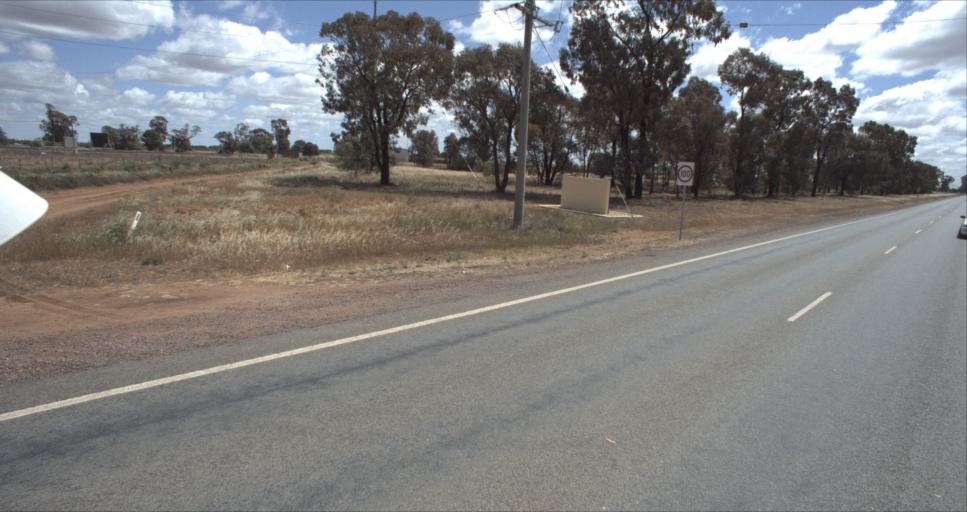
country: AU
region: New South Wales
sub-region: Murrumbidgee Shire
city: Darlington Point
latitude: -34.5099
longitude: 146.1865
